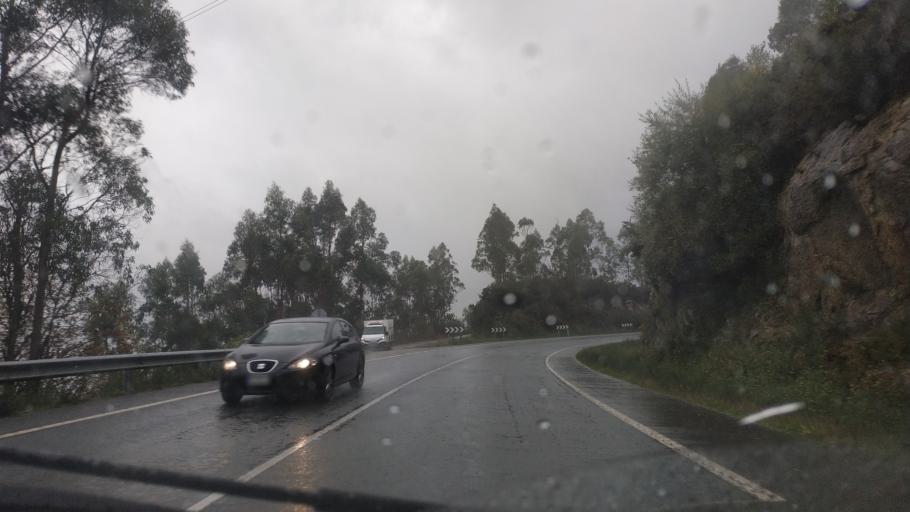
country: ES
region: Galicia
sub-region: Provincia da Coruna
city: Cerceda
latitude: 43.1703
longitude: -8.5093
